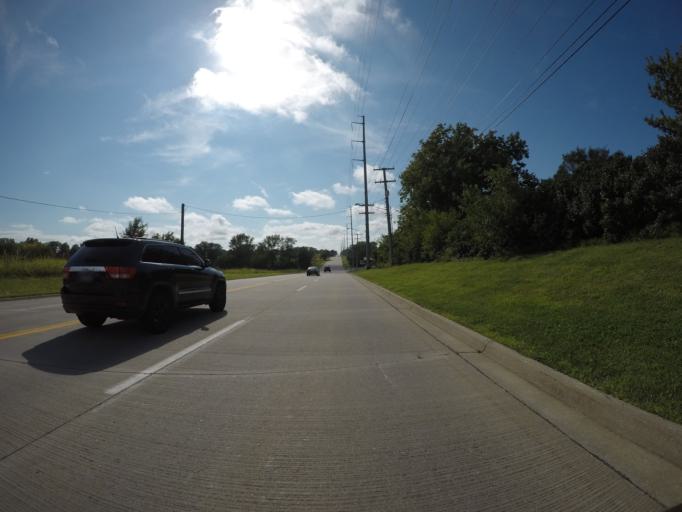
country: US
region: Kansas
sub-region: Wyandotte County
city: Edwardsville
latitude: 39.1287
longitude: -94.8441
